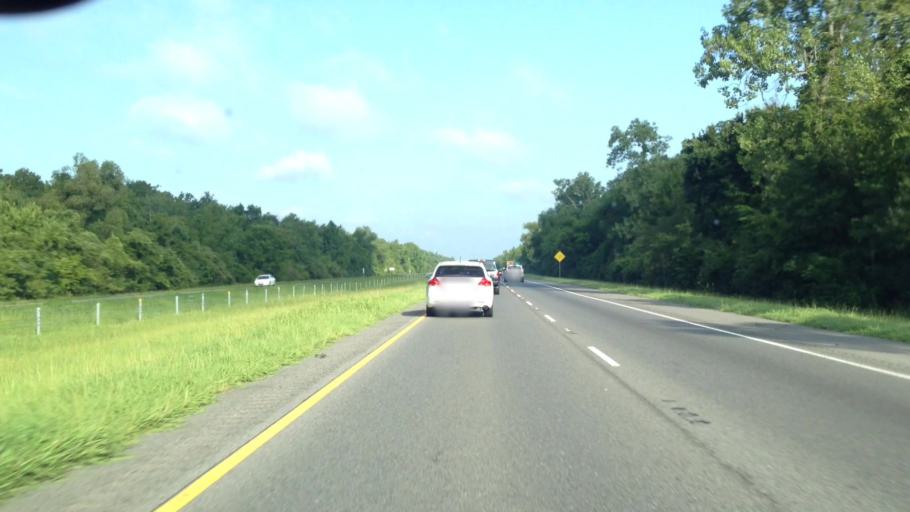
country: US
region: Louisiana
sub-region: Saint James Parish
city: Grand Point
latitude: 30.1429
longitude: -90.7567
